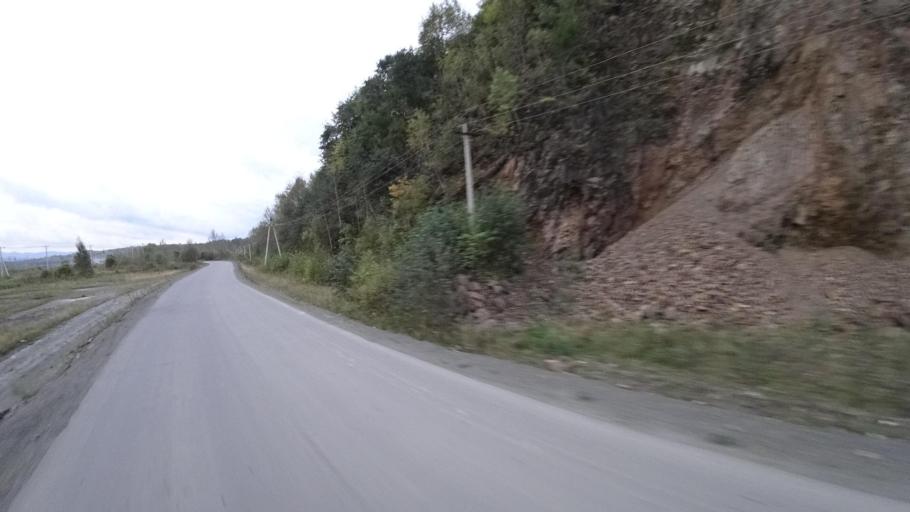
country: RU
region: Jewish Autonomous Oblast
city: Izvestkovyy
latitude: 48.9904
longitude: 131.5397
